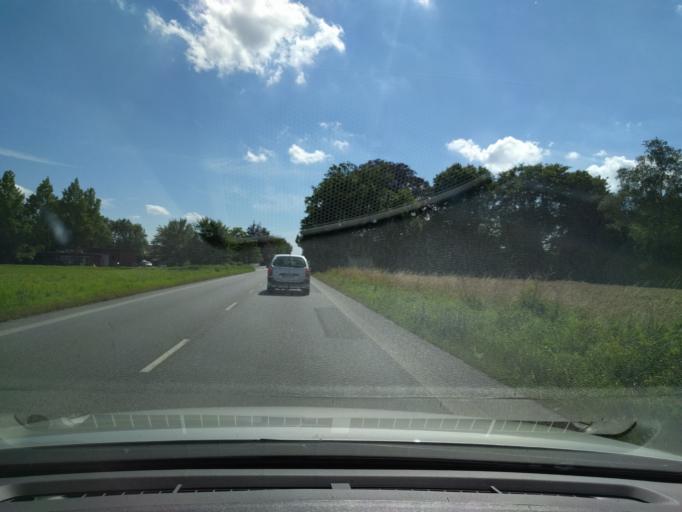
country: DK
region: Zealand
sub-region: Guldborgsund Kommune
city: Stubbekobing
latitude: 54.8666
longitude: 12.0215
